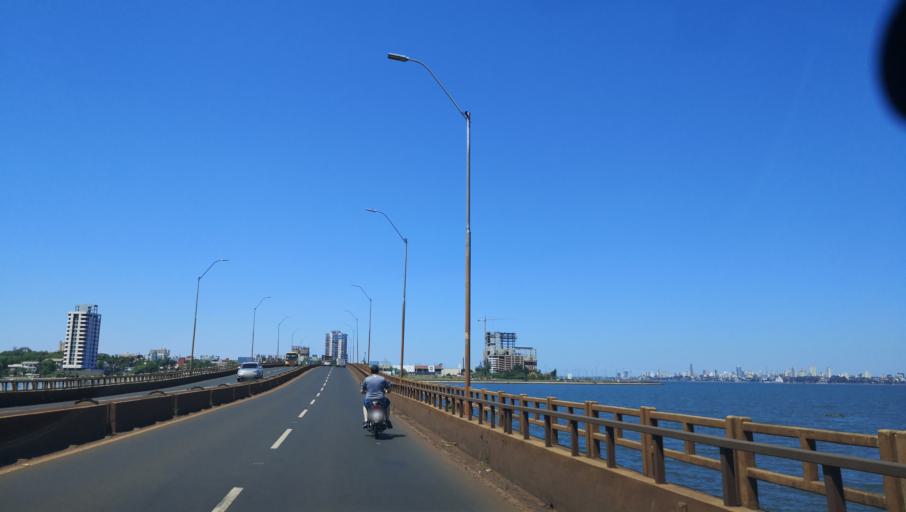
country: PY
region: Itapua
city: Encarnacion
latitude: -27.3165
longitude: -55.8752
